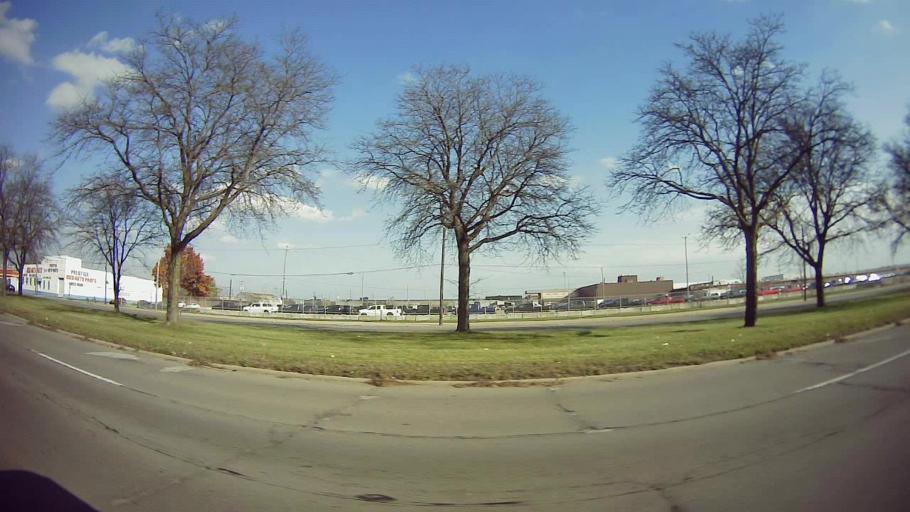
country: US
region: Michigan
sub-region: Macomb County
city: Warren
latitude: 42.4457
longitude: -83.0442
